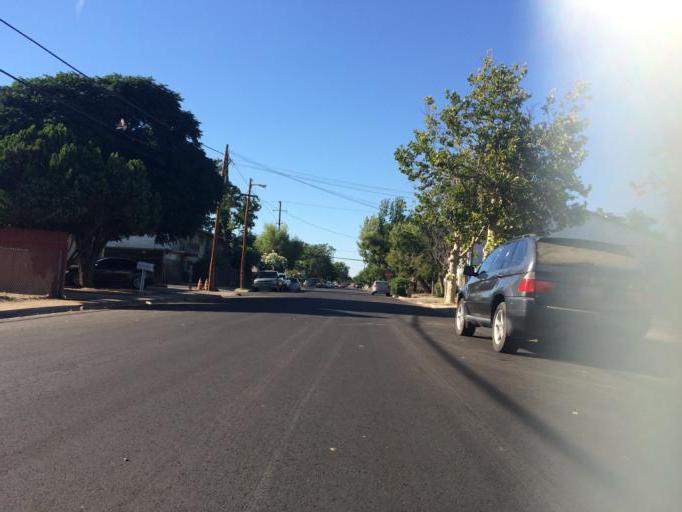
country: US
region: California
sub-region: Fresno County
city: Fresno
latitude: 36.7569
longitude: -119.7612
